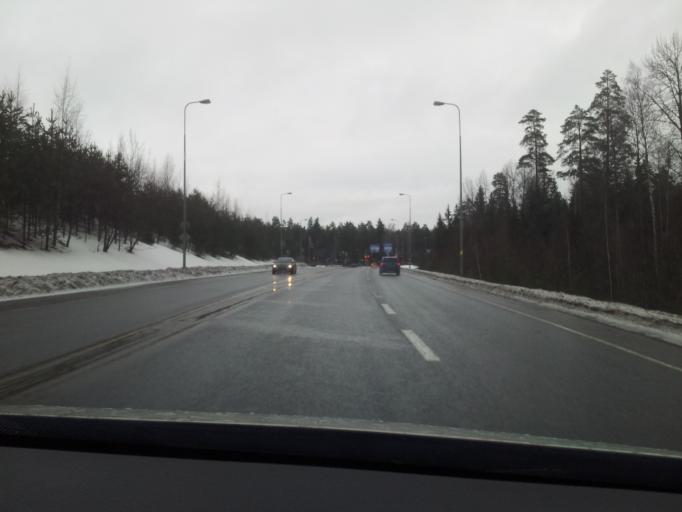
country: FI
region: Uusimaa
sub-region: Helsinki
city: Kauniainen
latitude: 60.2235
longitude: 24.7497
